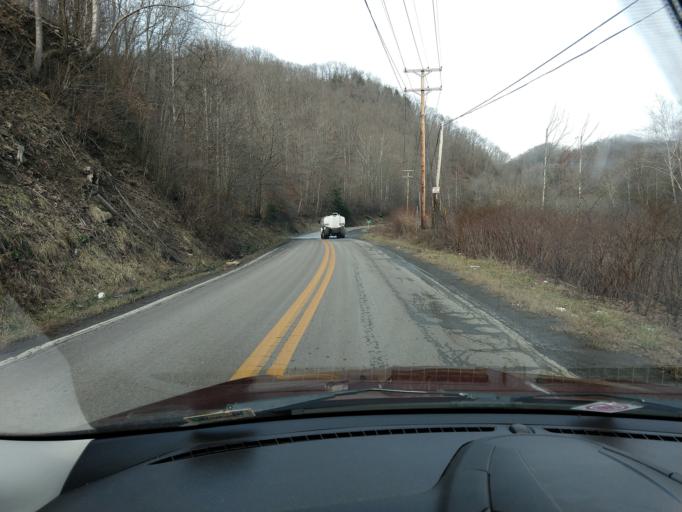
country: US
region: West Virginia
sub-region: McDowell County
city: Welch
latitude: 37.3266
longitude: -81.6880
